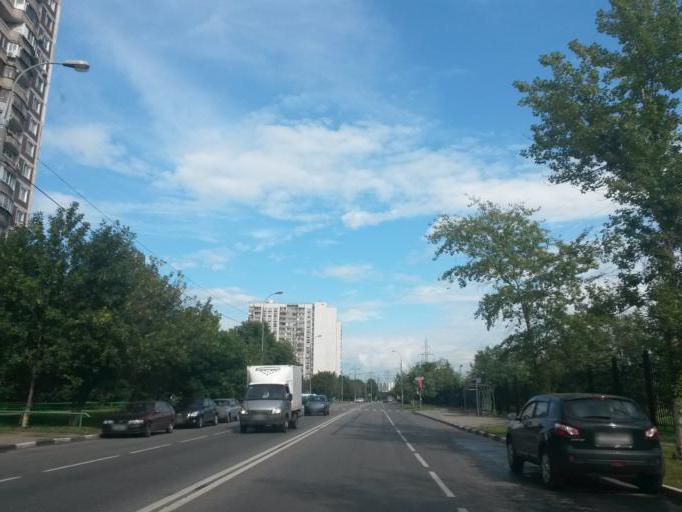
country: RU
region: Moscow
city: Mar'ino
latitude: 55.6434
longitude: 37.7337
